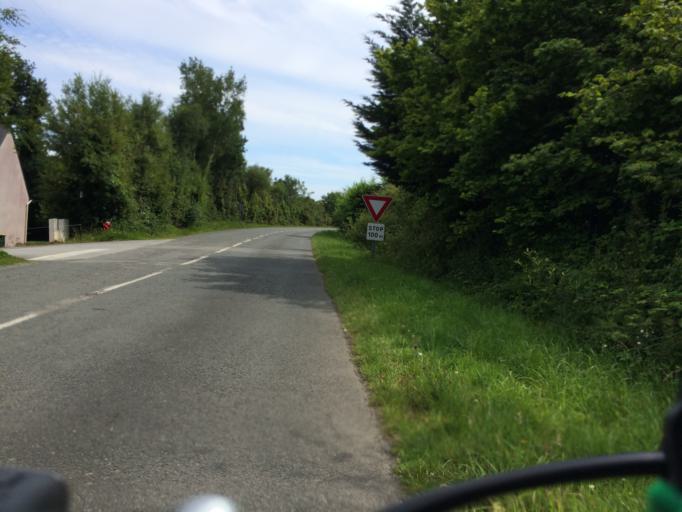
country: FR
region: Brittany
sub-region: Departement du Finistere
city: Logonna-Daoulas
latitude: 48.3207
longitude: -4.2960
